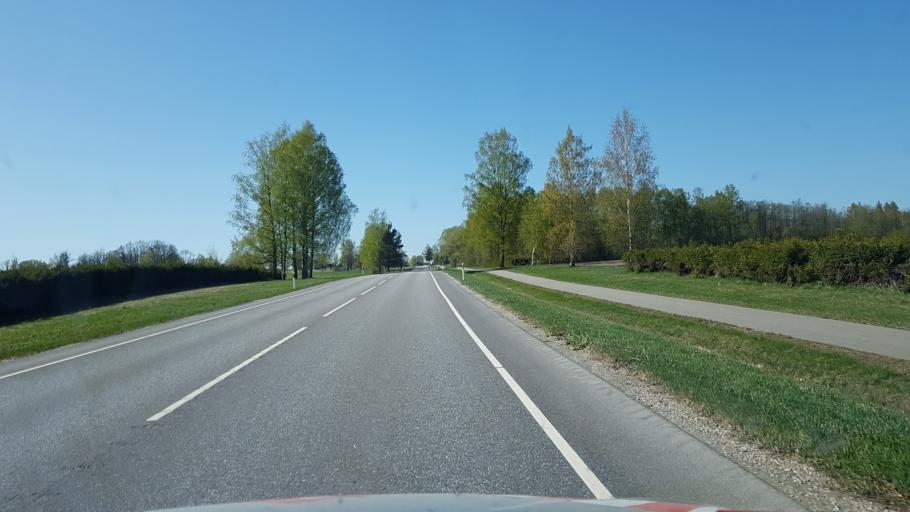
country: EE
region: Viljandimaa
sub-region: Karksi vald
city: Karksi-Nuia
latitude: 58.0852
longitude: 25.5884
